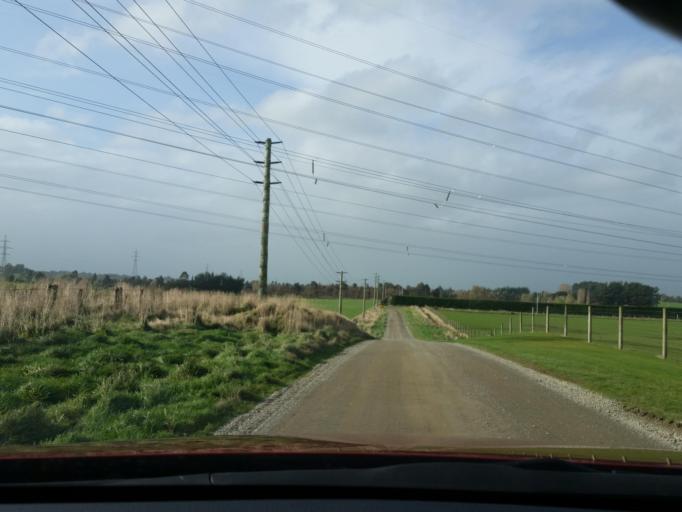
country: NZ
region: Southland
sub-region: Invercargill City
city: Invercargill
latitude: -46.3075
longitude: 168.3618
